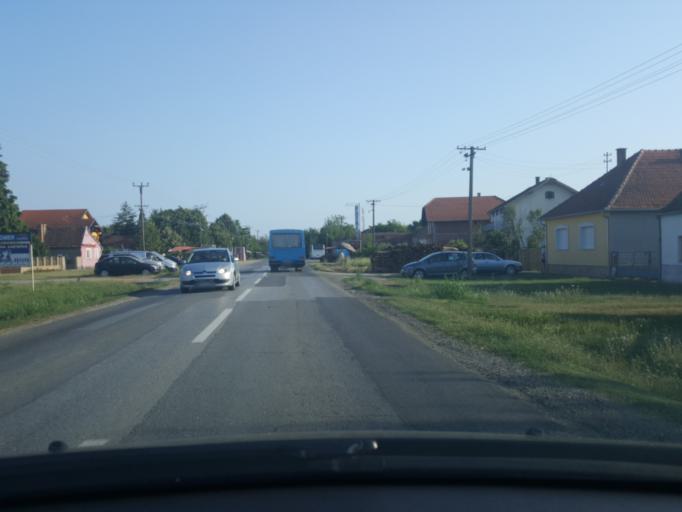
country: RS
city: Hrtkovci
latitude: 44.8889
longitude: 19.7638
